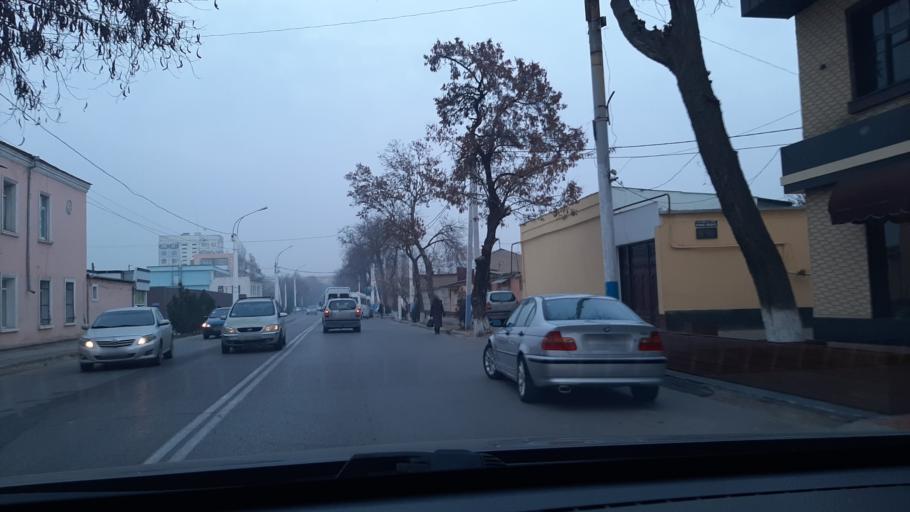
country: TJ
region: Viloyati Sughd
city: Khujand
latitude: 40.2777
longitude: 69.6125
